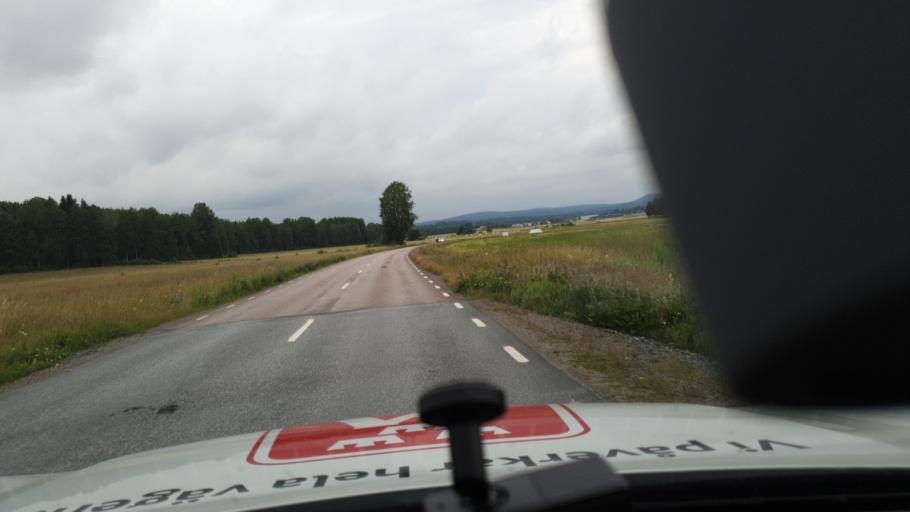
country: SE
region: Vaermland
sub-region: Sunne Kommun
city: Sunne
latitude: 59.8283
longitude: 13.1865
